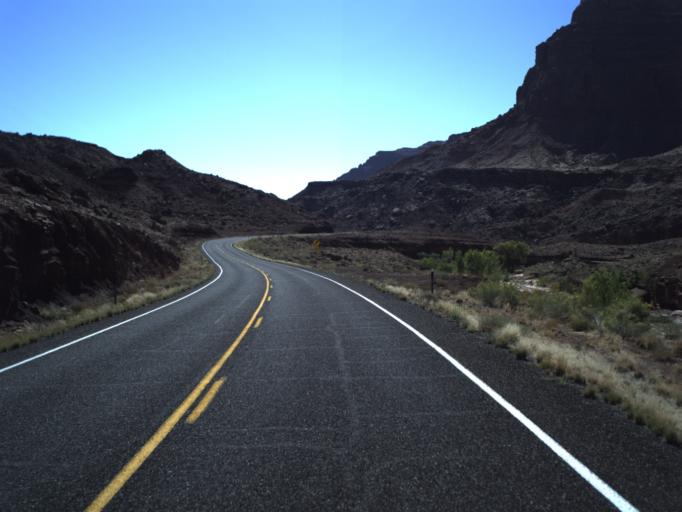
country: US
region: Utah
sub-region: San Juan County
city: Blanding
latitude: 37.8994
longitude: -110.4491
